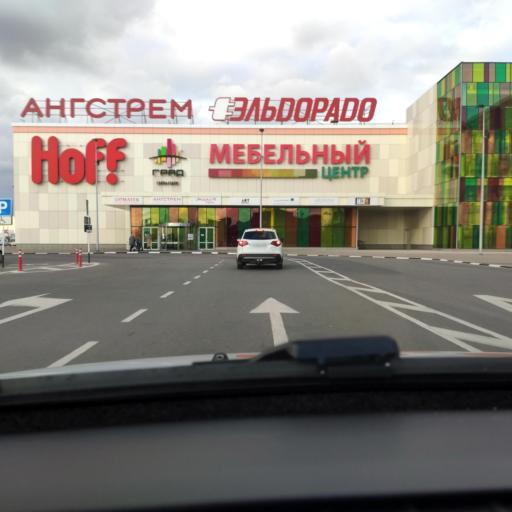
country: RU
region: Voronezj
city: Podgornoye
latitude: 51.7897
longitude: 39.2045
